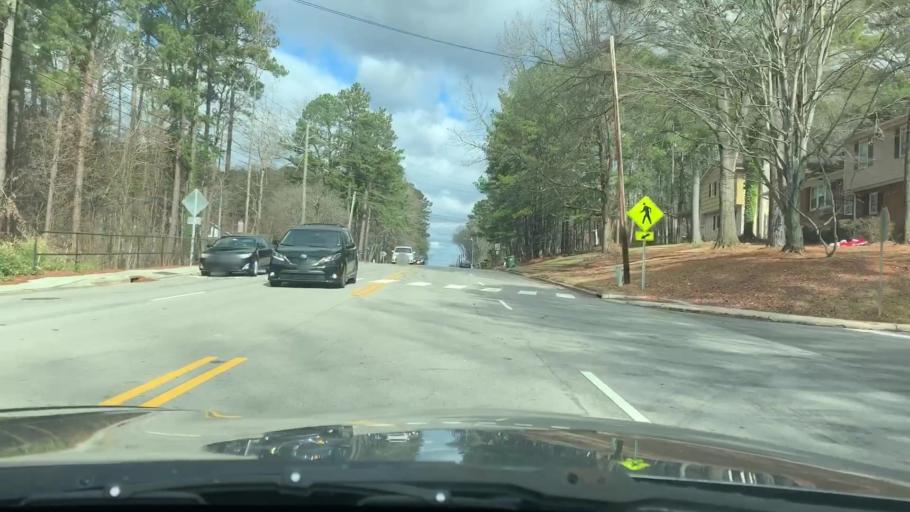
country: US
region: North Carolina
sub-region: Wake County
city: Cary
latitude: 35.7970
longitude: -78.7831
